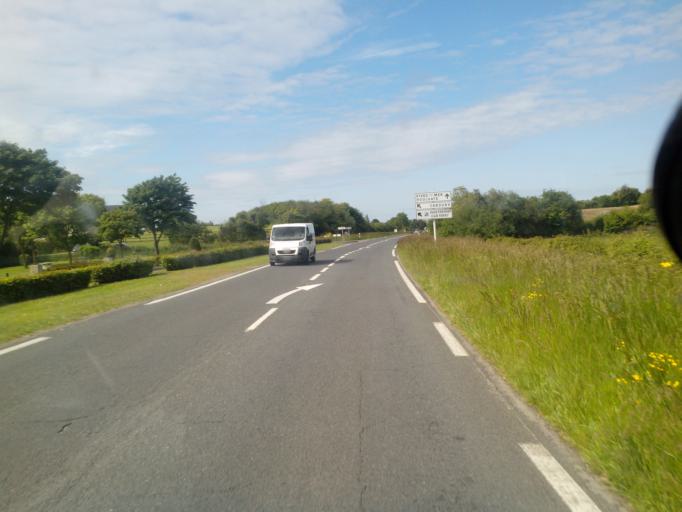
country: FR
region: Lower Normandy
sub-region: Departement du Calvados
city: Dives-sur-Mer
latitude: 49.2657
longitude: -0.1045
